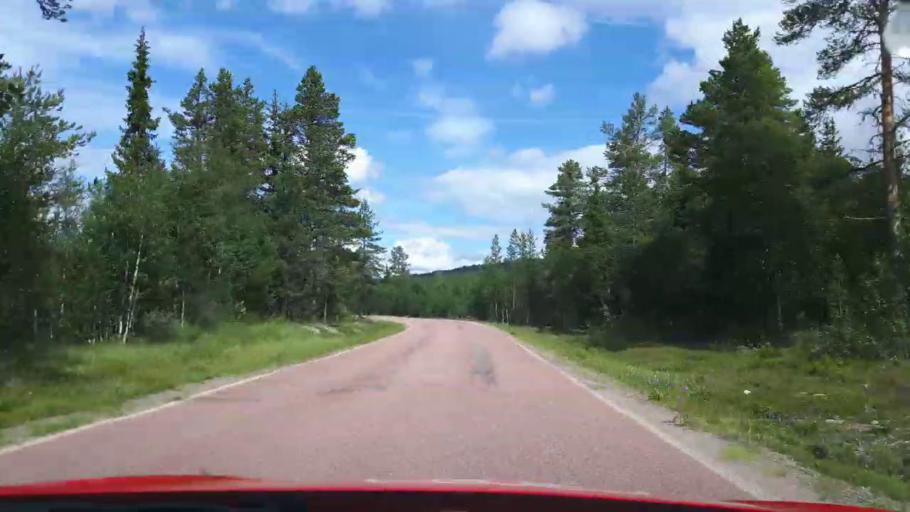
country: NO
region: Hedmark
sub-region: Trysil
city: Innbygda
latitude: 62.0144
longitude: 12.9770
